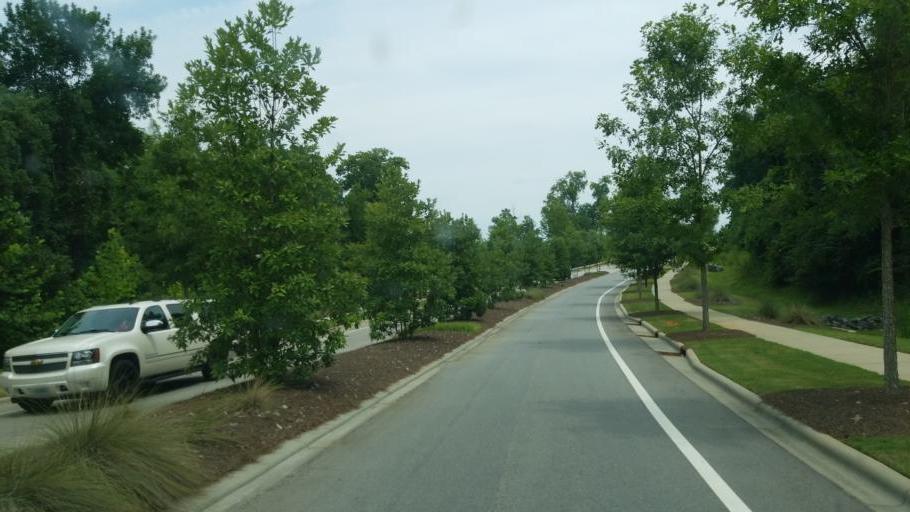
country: US
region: South Carolina
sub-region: York County
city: Fort Mill
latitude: 34.9818
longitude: -80.9756
